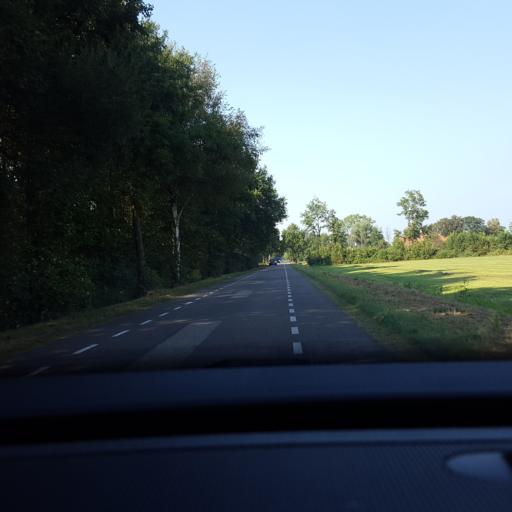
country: NL
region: Gelderland
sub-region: Oude IJsselstreek
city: Varsseveld
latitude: 52.0227
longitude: 6.4574
